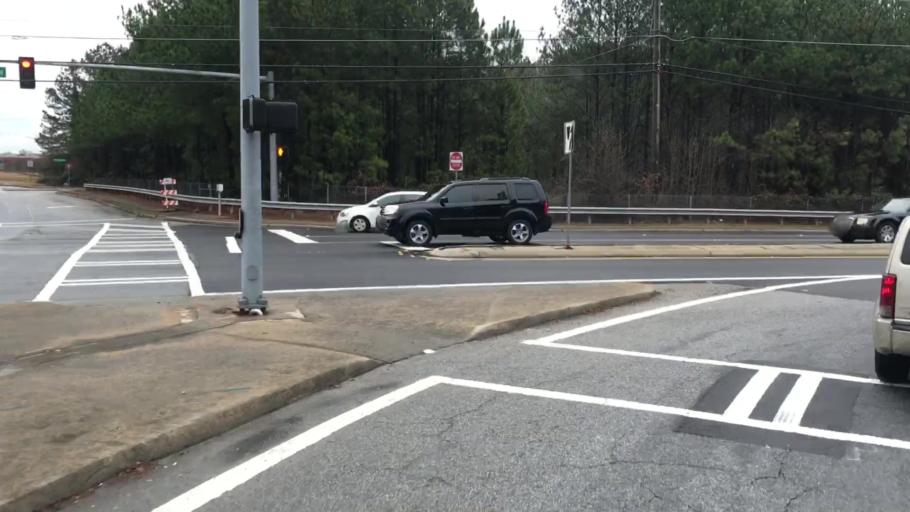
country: US
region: Georgia
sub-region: Gwinnett County
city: Snellville
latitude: 33.8526
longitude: -84.0192
